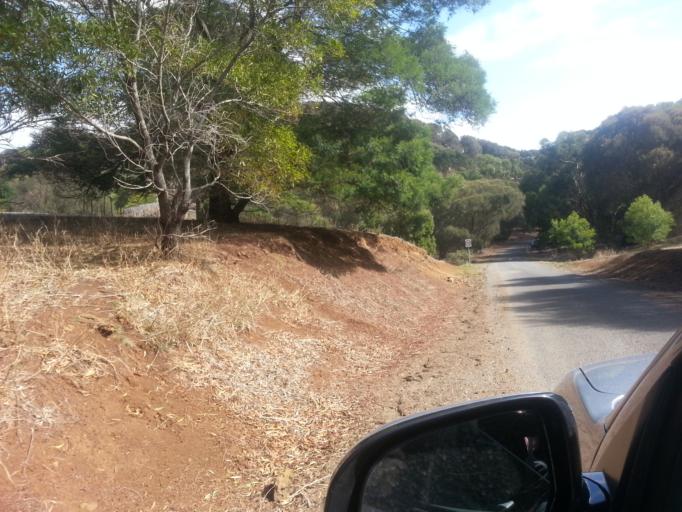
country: AU
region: Victoria
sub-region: Warrnambool
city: Warrnambool
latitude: -38.3212
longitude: 142.3645
